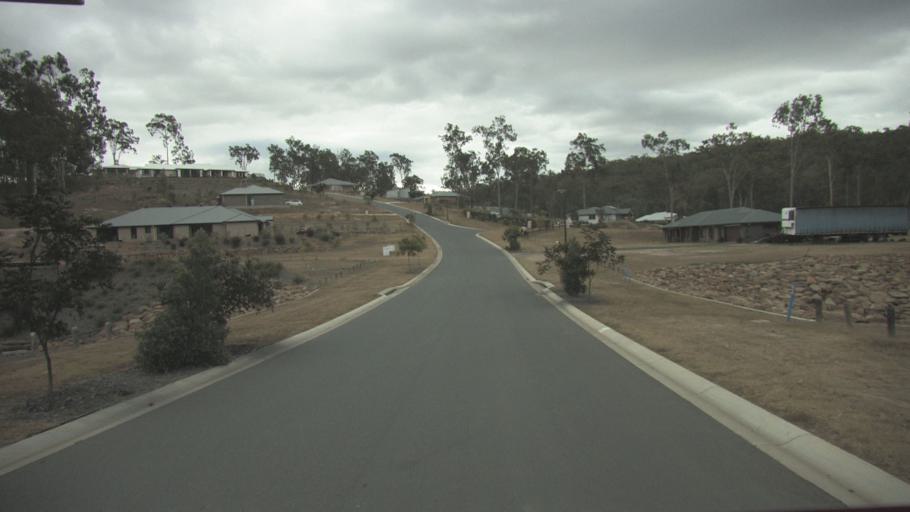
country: AU
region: Queensland
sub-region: Logan
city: Cedar Vale
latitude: -27.8613
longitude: 153.0784
